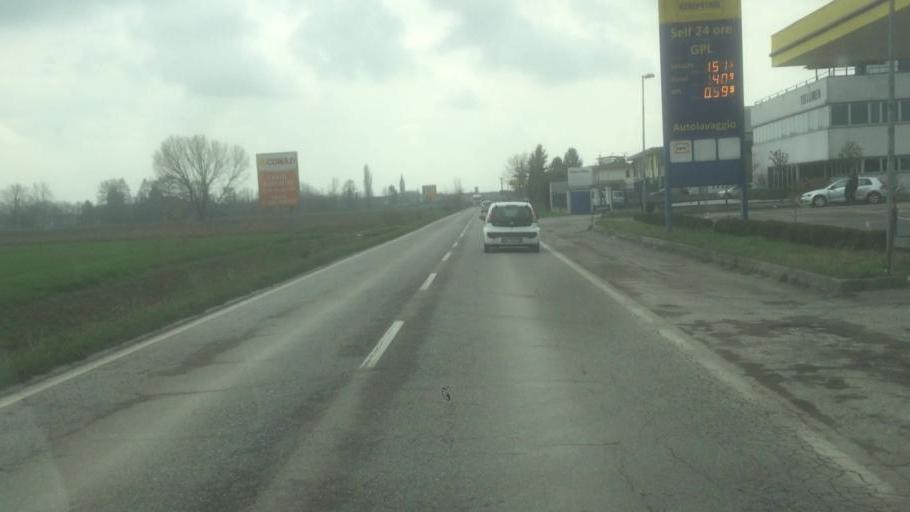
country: IT
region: Lombardy
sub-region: Provincia di Mantova
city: Casaloldo
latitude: 45.2646
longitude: 10.4773
